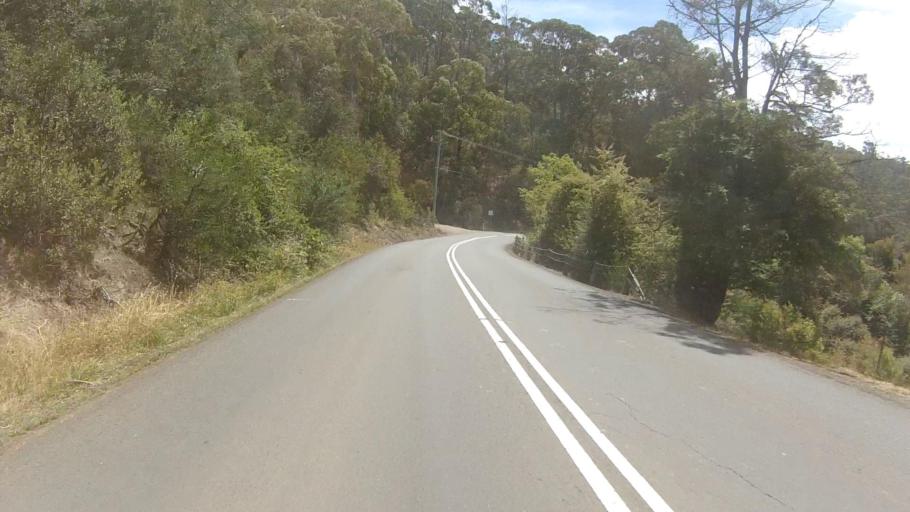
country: AU
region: Tasmania
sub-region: Kingborough
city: Kingston Beach
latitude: -42.9622
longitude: 147.3311
